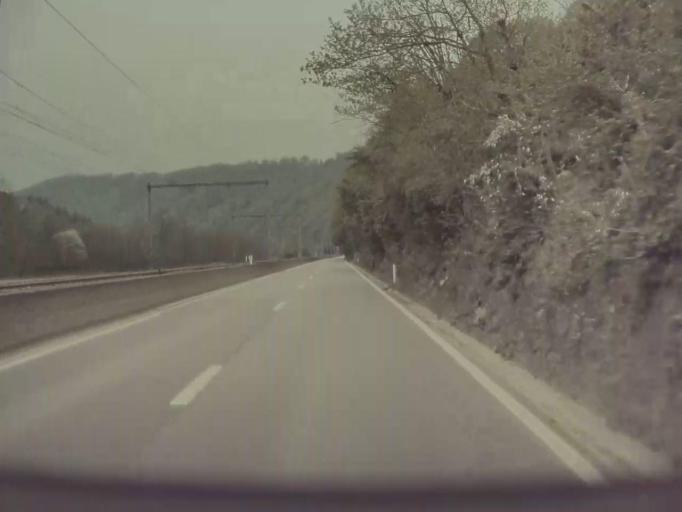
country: BE
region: Wallonia
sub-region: Province de Liege
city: Hamoir
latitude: 50.4217
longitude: 5.5226
